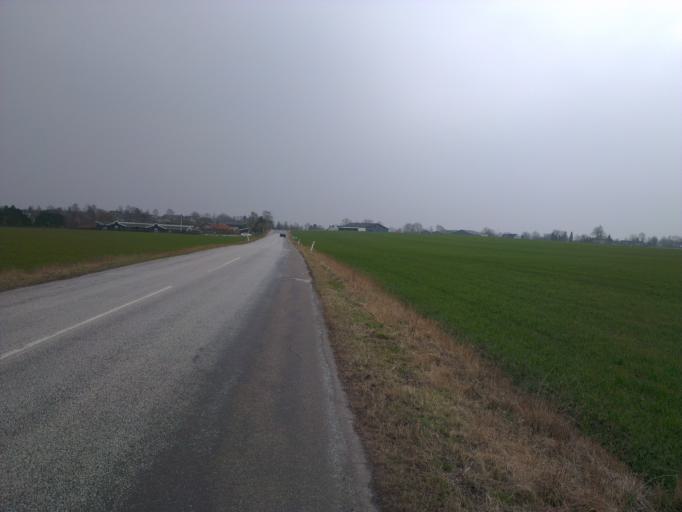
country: DK
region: Zealand
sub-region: Roskilde Kommune
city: Jyllinge
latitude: 55.8030
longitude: 12.1110
